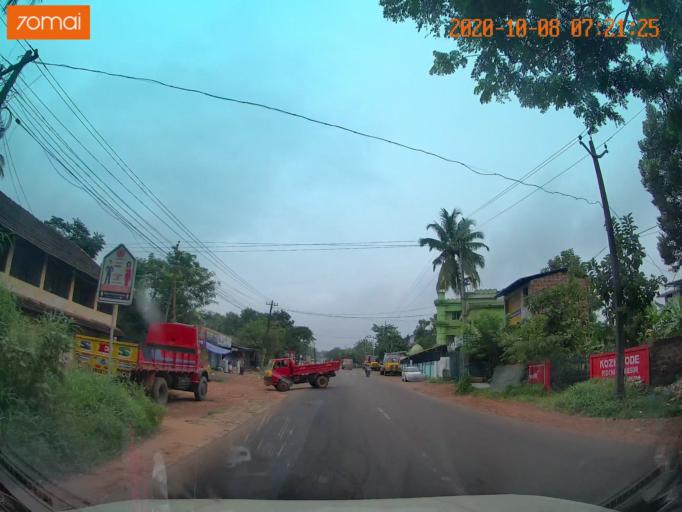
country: IN
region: Kerala
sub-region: Malappuram
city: Tirur
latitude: 10.8553
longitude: 76.0366
